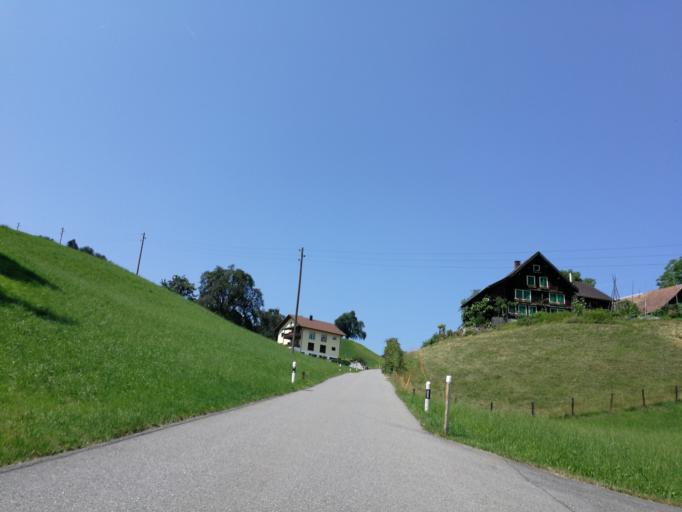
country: CH
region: Schwyz
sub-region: Bezirk March
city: Altendorf
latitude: 47.1874
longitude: 8.8160
